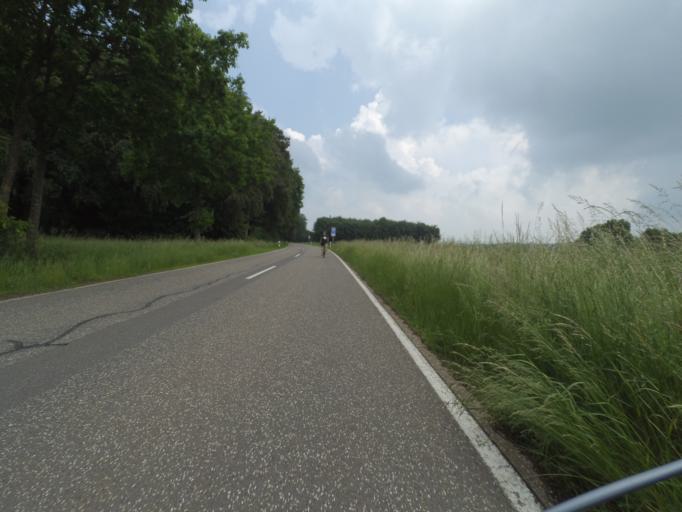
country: DE
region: Rheinland-Pfalz
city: Reidenhausen
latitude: 50.0591
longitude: 7.3260
